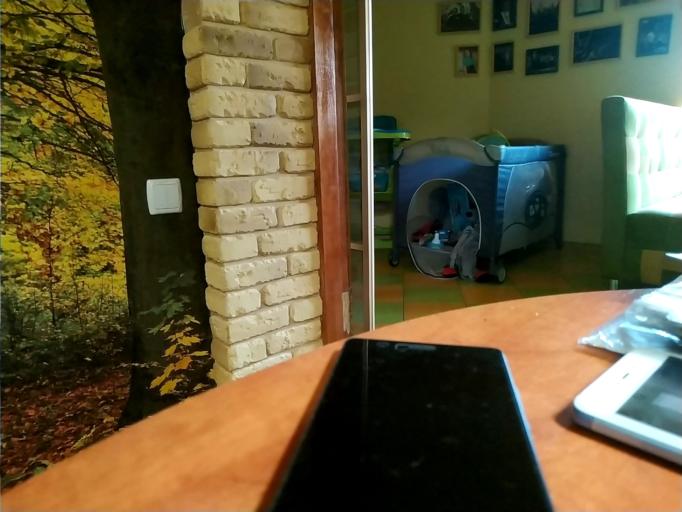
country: RU
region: Kaluga
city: Seredeyskiy
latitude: 53.7811
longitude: 35.4006
